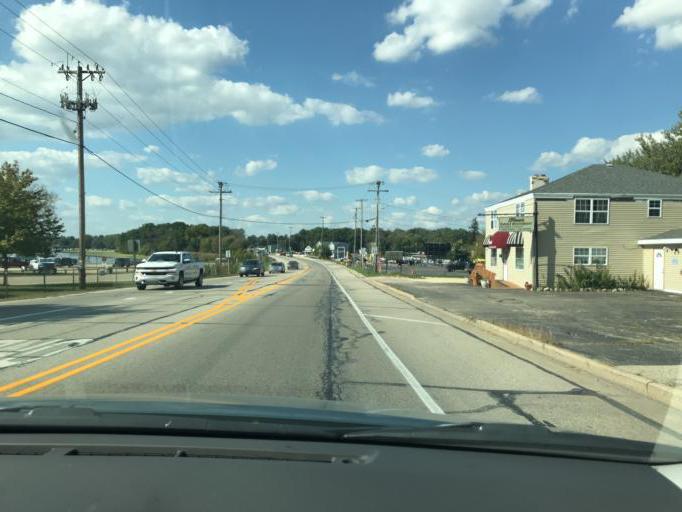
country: US
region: Wisconsin
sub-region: Walworth County
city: Williams Bay
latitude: 42.6193
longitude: -88.5812
